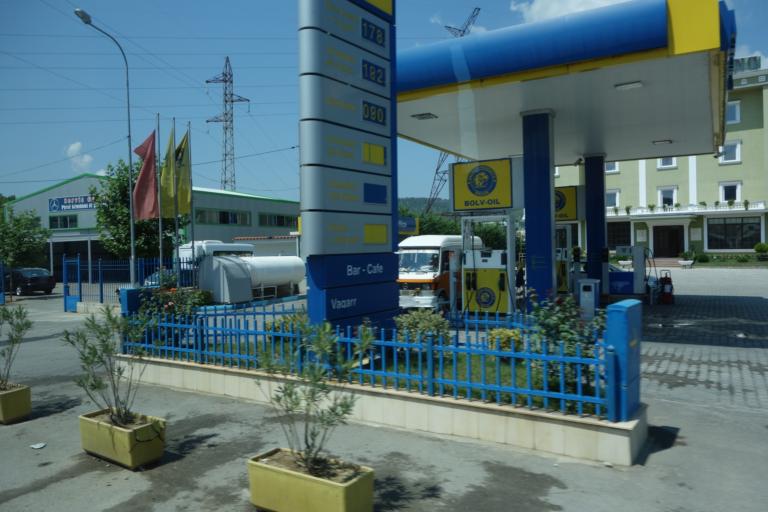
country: AL
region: Tirane
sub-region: Rrethi i Tiranes
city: Vaqarr
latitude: 41.3074
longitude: 19.7578
